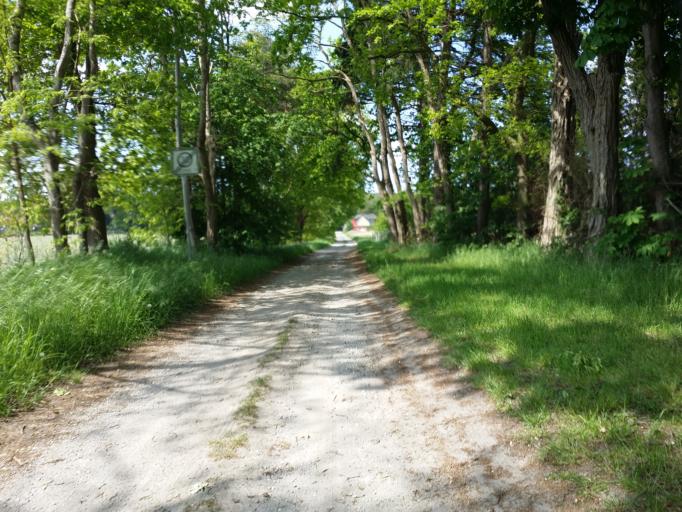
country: DE
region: Lower Saxony
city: Hambergen
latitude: 53.2928
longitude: 8.8374
